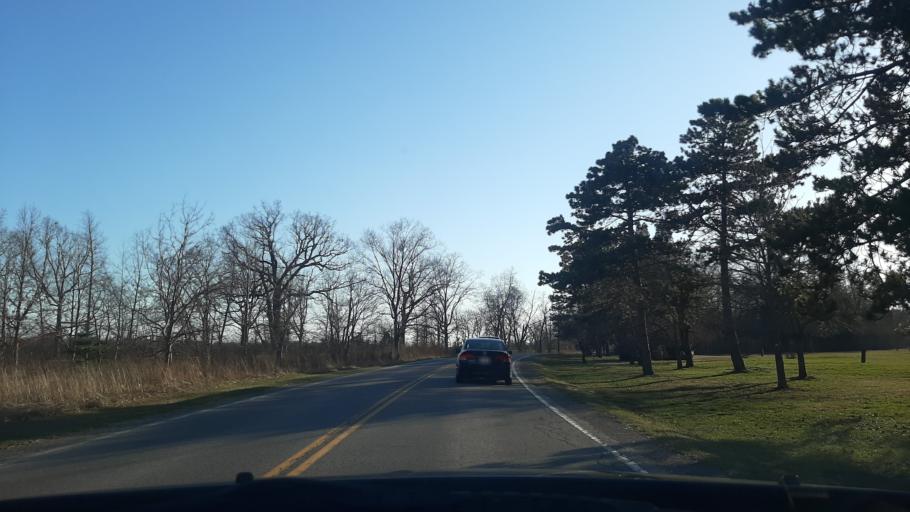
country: US
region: New York
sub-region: Niagara County
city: Lewiston
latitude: 43.1391
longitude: -79.0477
